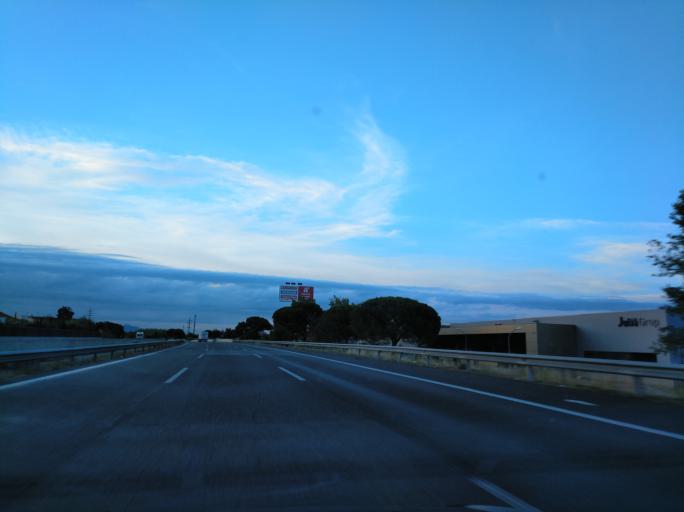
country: ES
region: Catalonia
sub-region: Provincia de Girona
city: Sils
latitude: 41.8069
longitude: 2.7491
